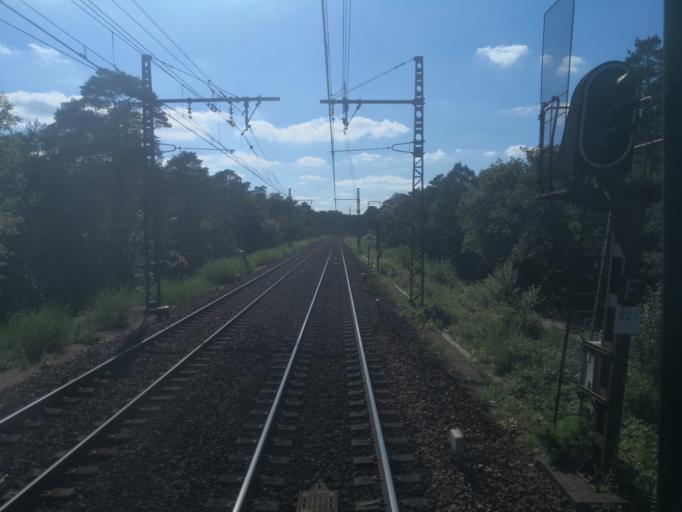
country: FR
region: Ile-de-France
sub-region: Departement de Seine-et-Marne
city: Avon
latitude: 48.3955
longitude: 2.7503
